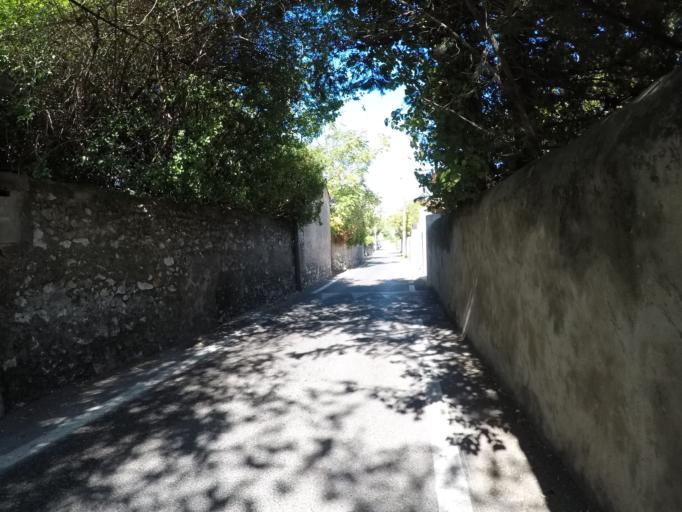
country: FR
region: Provence-Alpes-Cote d'Azur
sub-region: Departement des Bouches-du-Rhone
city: Marseille 09
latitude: 43.2421
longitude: 5.4046
